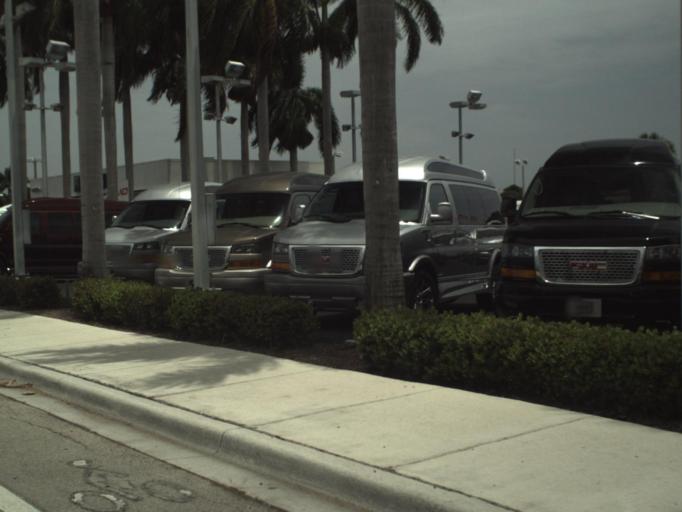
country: US
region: Florida
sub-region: Broward County
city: Lighthouse Point
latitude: 26.2648
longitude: -80.0988
